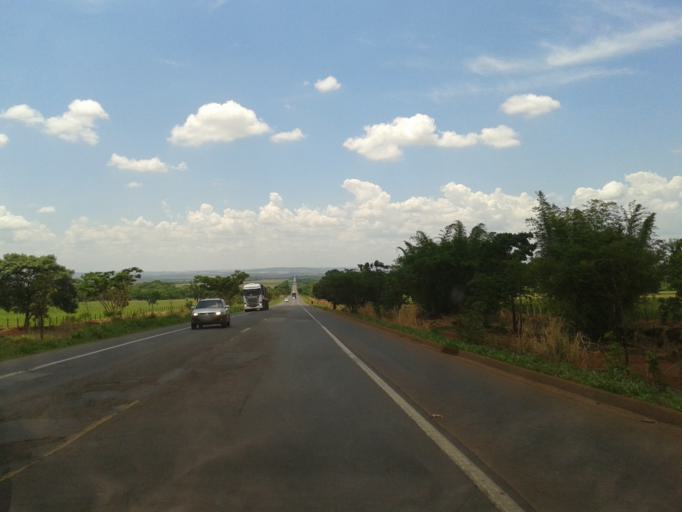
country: BR
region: Goias
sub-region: Goiatuba
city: Goiatuba
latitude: -18.2605
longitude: -49.6665
